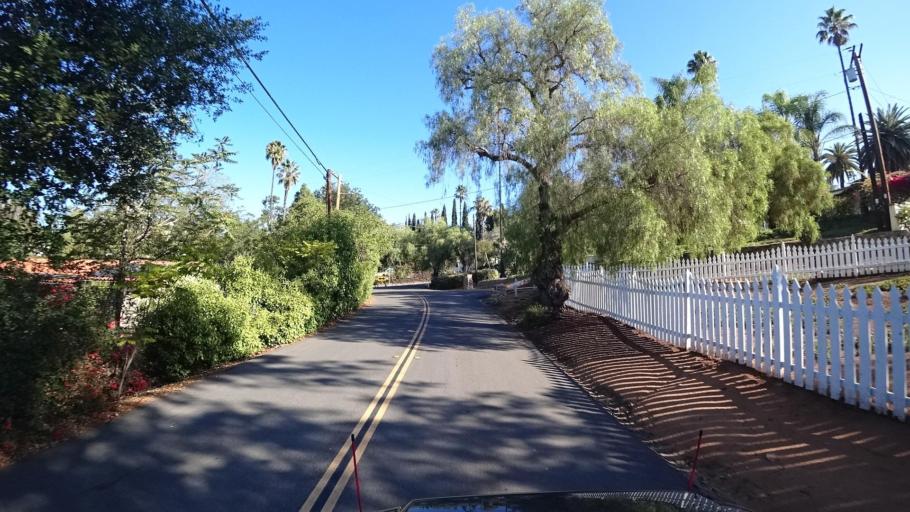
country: US
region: California
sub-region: San Diego County
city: La Mesa
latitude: 32.7732
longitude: -116.9955
